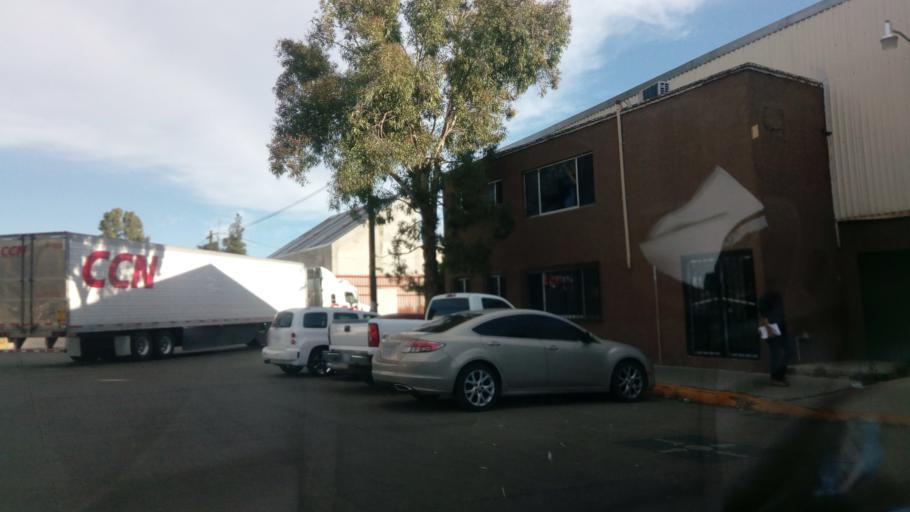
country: MX
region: Durango
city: Victoria de Durango
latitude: 24.0671
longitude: -104.6081
